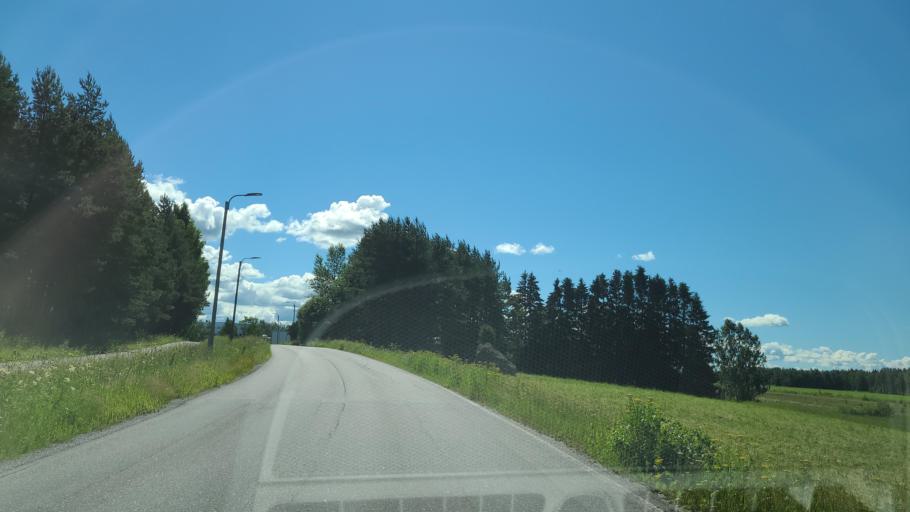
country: FI
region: Ostrobothnia
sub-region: Vaasa
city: Ristinummi
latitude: 63.0627
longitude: 21.7262
